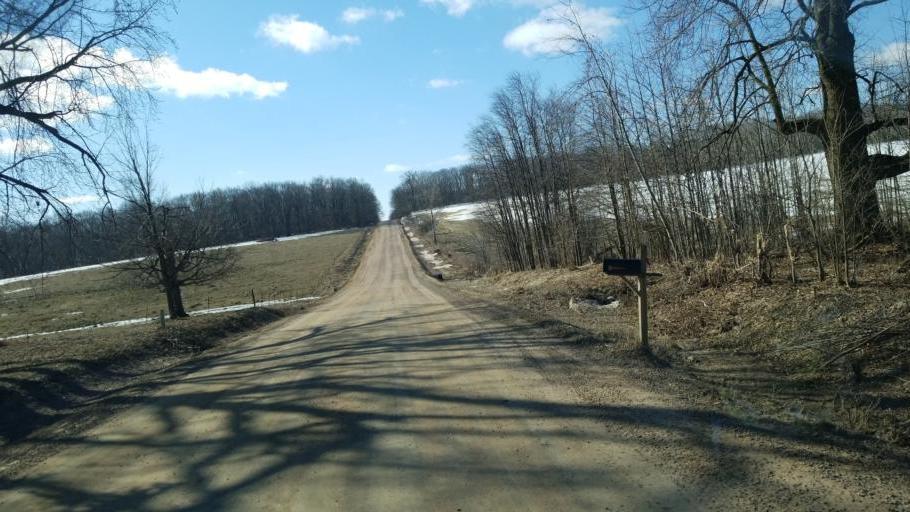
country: US
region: Wisconsin
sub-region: Clark County
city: Loyal
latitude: 44.6653
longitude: -90.4559
